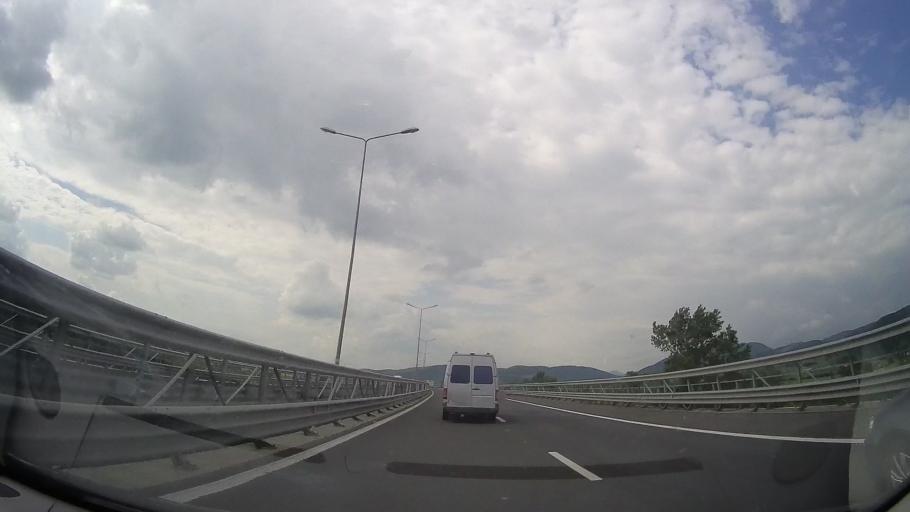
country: RO
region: Hunedoara
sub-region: Oras Simeria
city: Simeria
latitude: 45.8653
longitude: 23.0244
